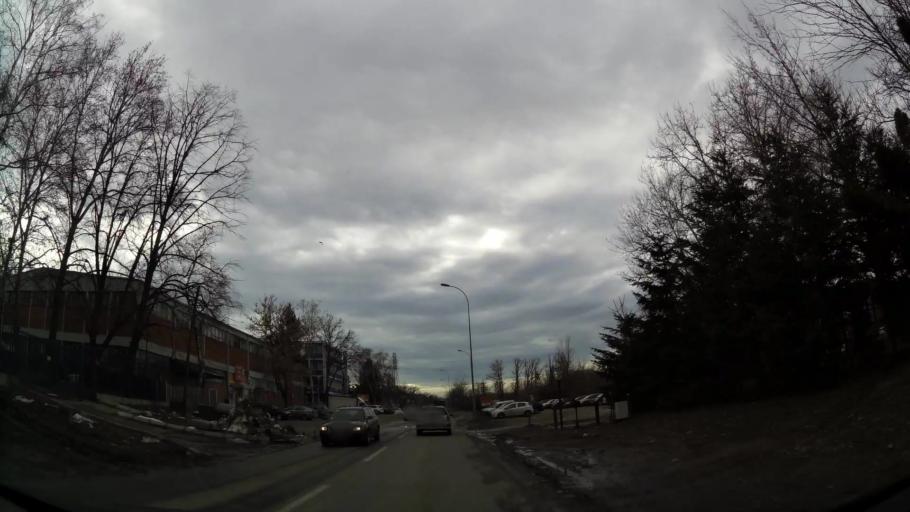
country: RS
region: Central Serbia
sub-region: Belgrade
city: Cukarica
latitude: 44.7675
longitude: 20.4068
